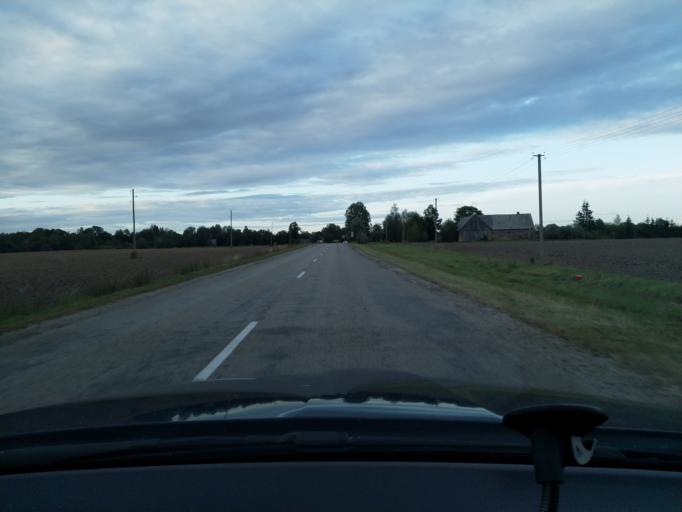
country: LV
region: Talsu Rajons
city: Sabile
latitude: 56.9574
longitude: 22.6125
